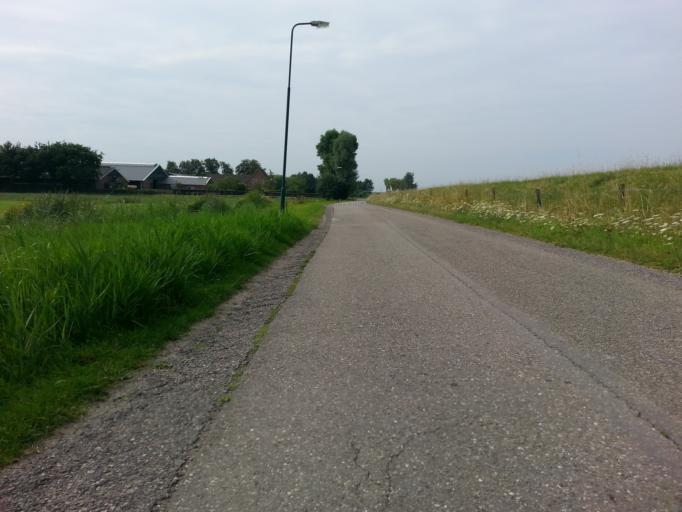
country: NL
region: Utrecht
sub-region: Gemeente Baarn
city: Baarn
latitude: 52.2117
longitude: 5.3113
